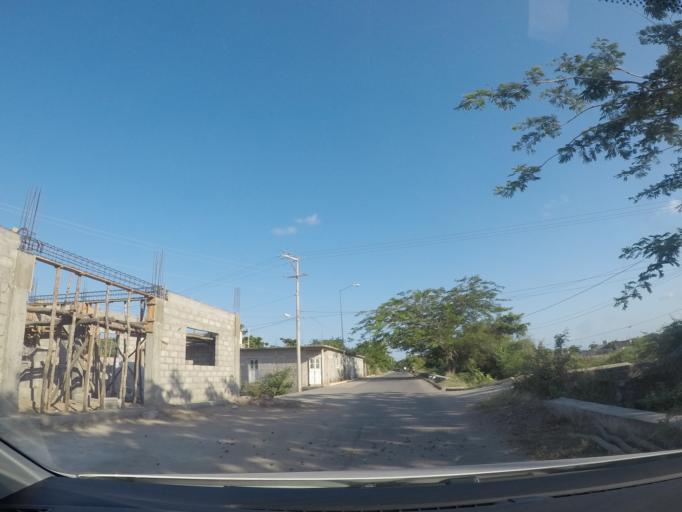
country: MX
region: Oaxaca
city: Juchitan de Zaragoza
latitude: 16.4195
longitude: -95.0271
